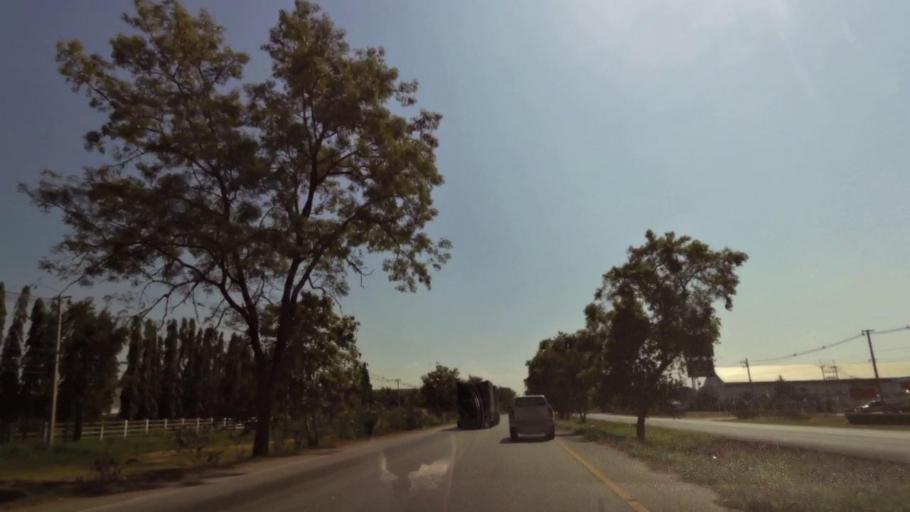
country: TH
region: Nakhon Sawan
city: Kao Liao
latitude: 15.8220
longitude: 100.1193
